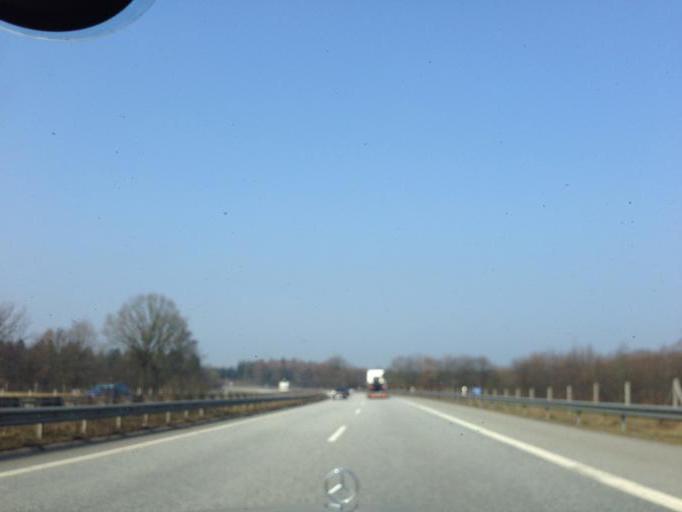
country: DE
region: Schleswig-Holstein
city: Daldorf
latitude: 54.0234
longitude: 10.2448
